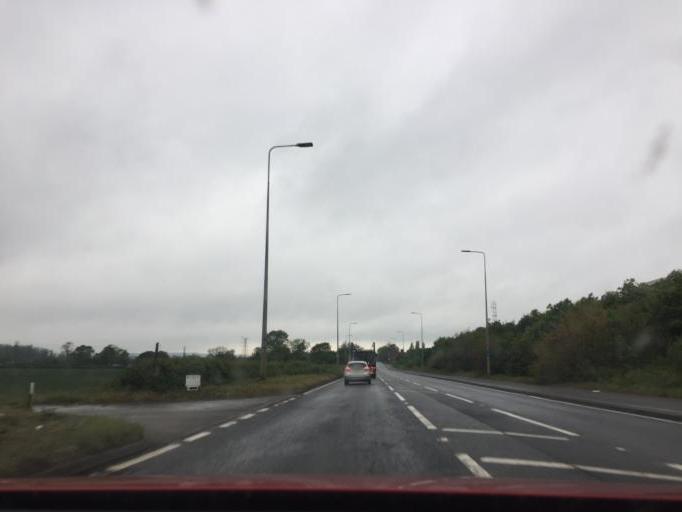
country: GB
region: England
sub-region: Leicestershire
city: Hinckley
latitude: 52.5258
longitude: -1.3898
